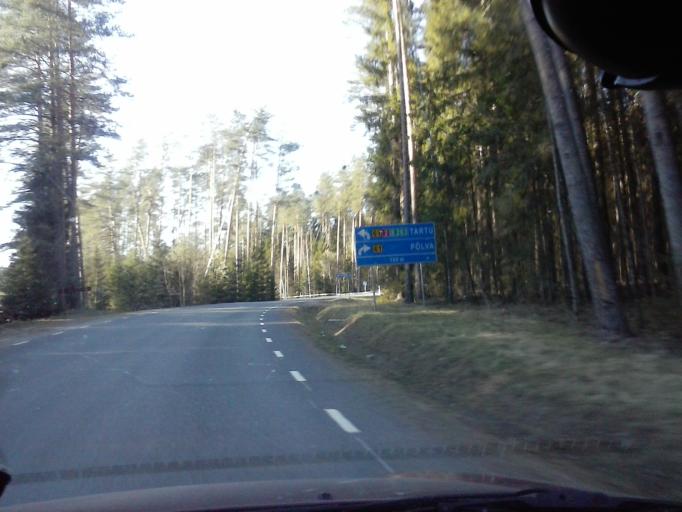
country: EE
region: Tartu
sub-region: UElenurme vald
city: Ulenurme
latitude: 58.1788
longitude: 26.8281
